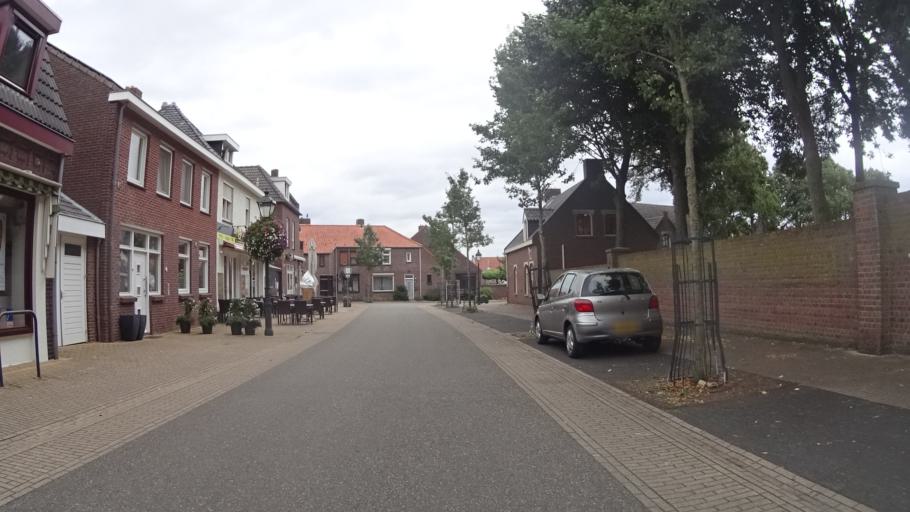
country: NL
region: Limburg
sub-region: Gemeente Beesel
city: Reuver
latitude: 51.2914
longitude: 6.0559
